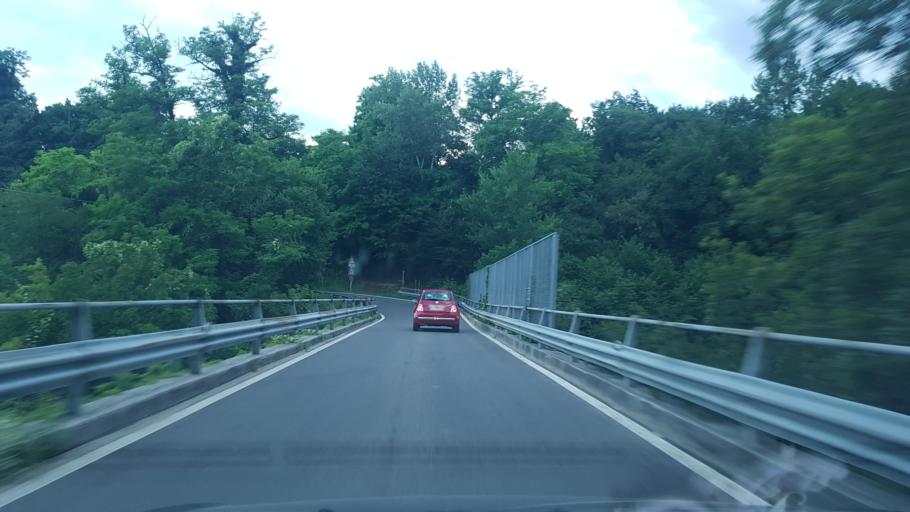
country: IT
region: Friuli Venezia Giulia
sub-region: Provincia di Pordenone
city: Pinzano al Tagliamento
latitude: 46.1836
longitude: 12.9526
